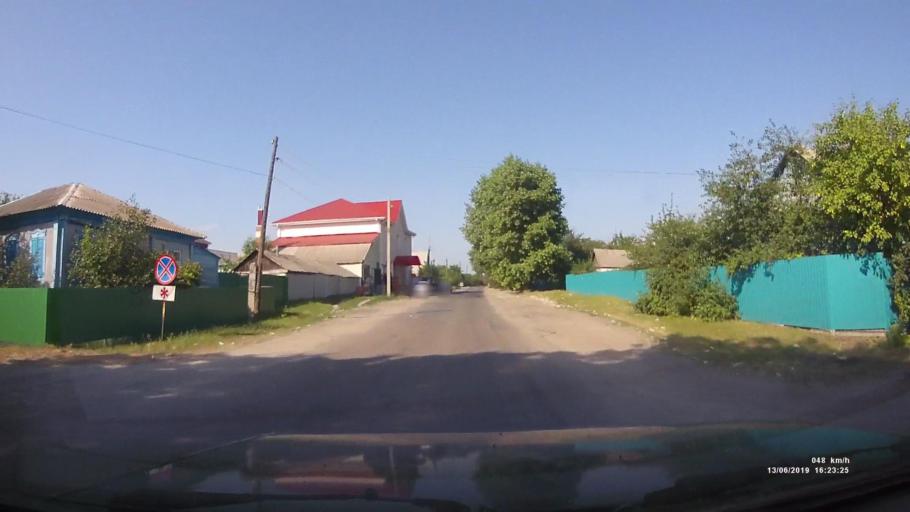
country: RU
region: Rostov
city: Kazanskaya
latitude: 49.7940
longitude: 41.1398
